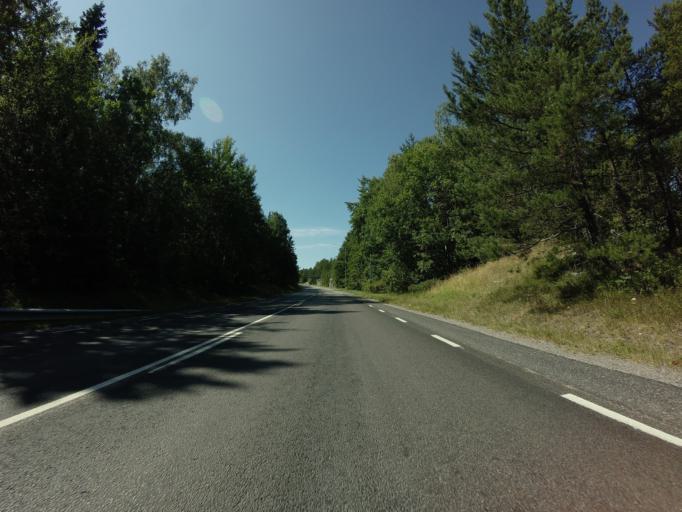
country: SE
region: Stockholm
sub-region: Lidingo
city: Brevik
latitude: 59.3505
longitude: 18.2024
